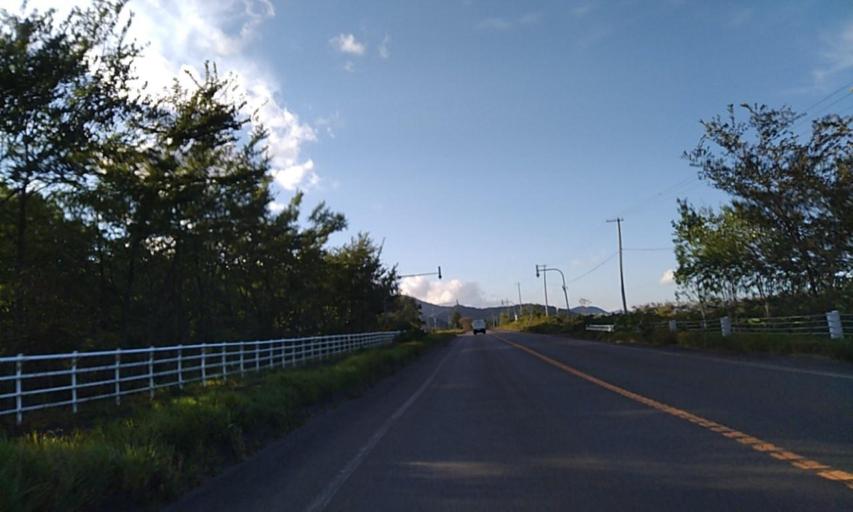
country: JP
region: Hokkaido
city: Otofuke
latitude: 42.9844
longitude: 142.8586
